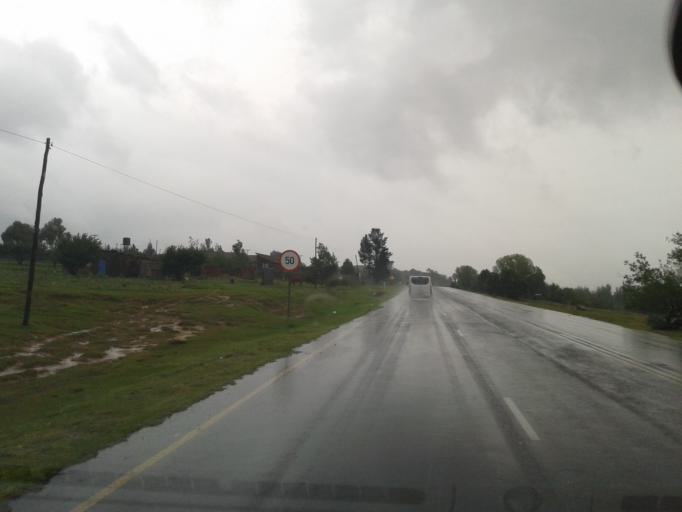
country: LS
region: Maseru
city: Nako
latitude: -29.6400
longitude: 27.4771
